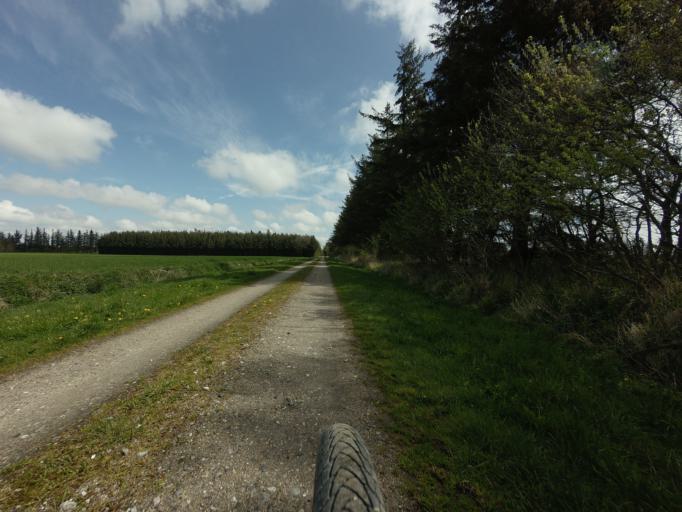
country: DK
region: North Denmark
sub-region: Jammerbugt Kommune
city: Kas
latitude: 57.1980
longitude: 9.5963
